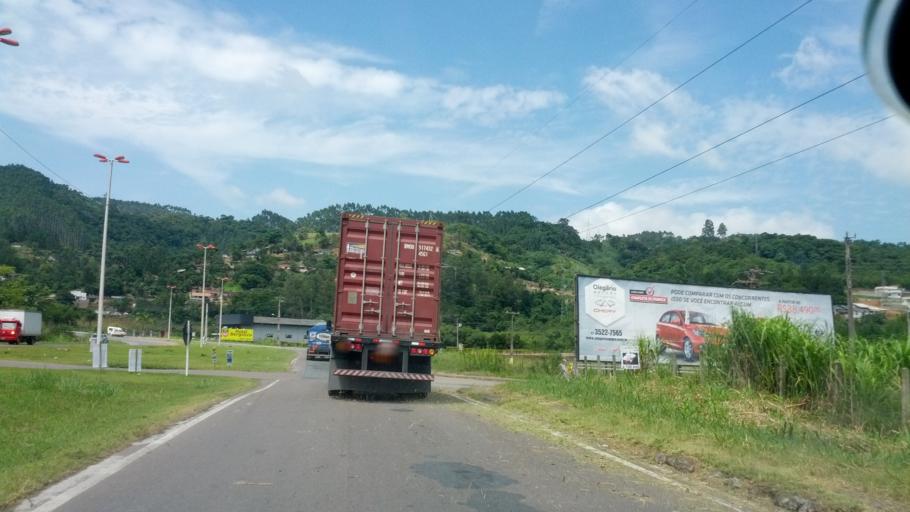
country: BR
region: Santa Catarina
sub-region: Ibirama
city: Ibirama
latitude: -27.0816
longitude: -49.5206
